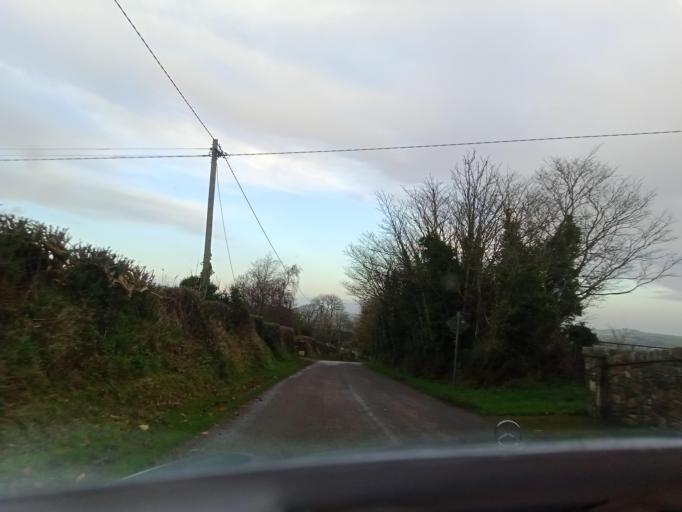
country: IE
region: Leinster
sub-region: Loch Garman
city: New Ross
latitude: 52.3429
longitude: -7.0318
